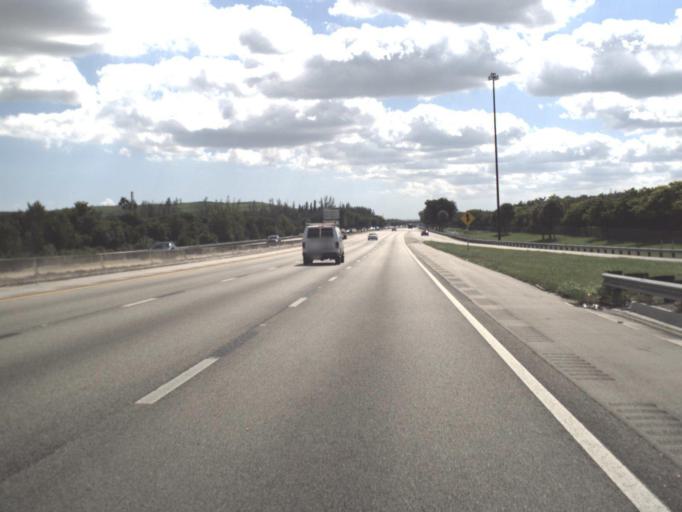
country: US
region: Florida
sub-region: Palm Beach County
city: Boca Pointe
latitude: 26.3022
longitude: -80.1695
